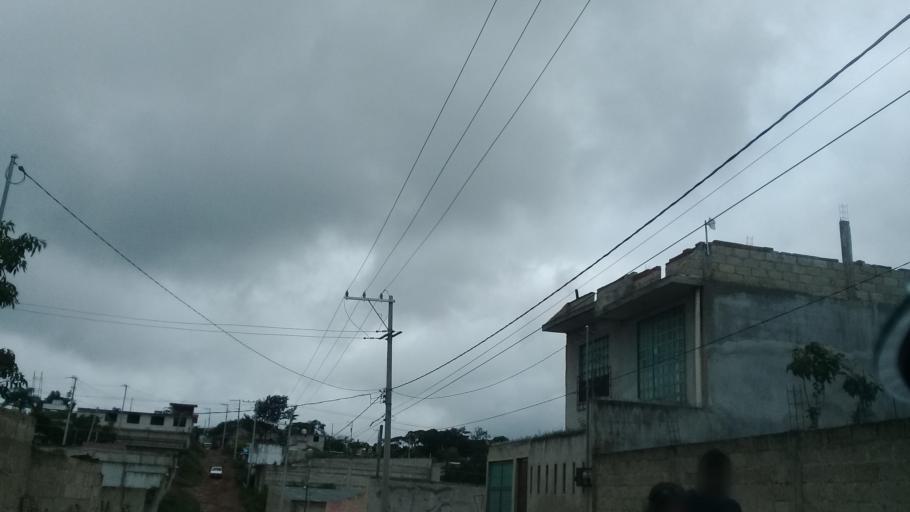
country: MX
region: Veracruz
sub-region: Emiliano Zapata
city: Las Trancas
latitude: 19.4966
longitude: -96.8634
